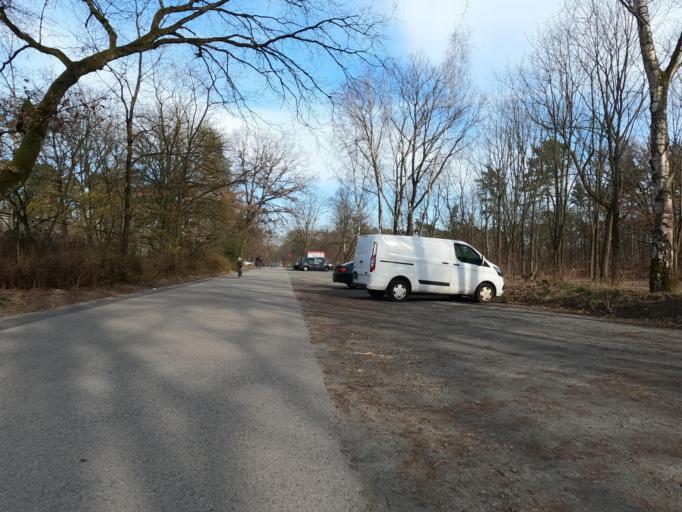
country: DE
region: Hesse
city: Raunheim
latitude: 50.0105
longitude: 8.4723
